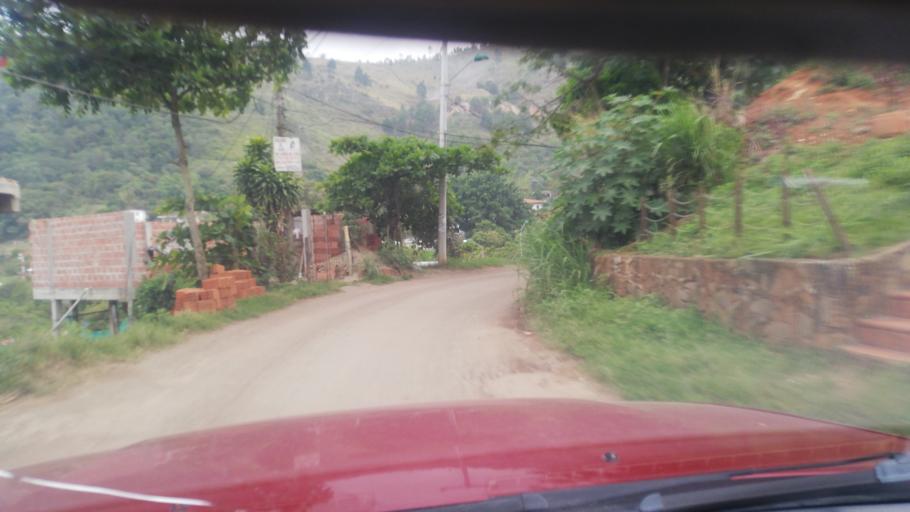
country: CO
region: Valle del Cauca
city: Cali
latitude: 3.4975
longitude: -76.5492
